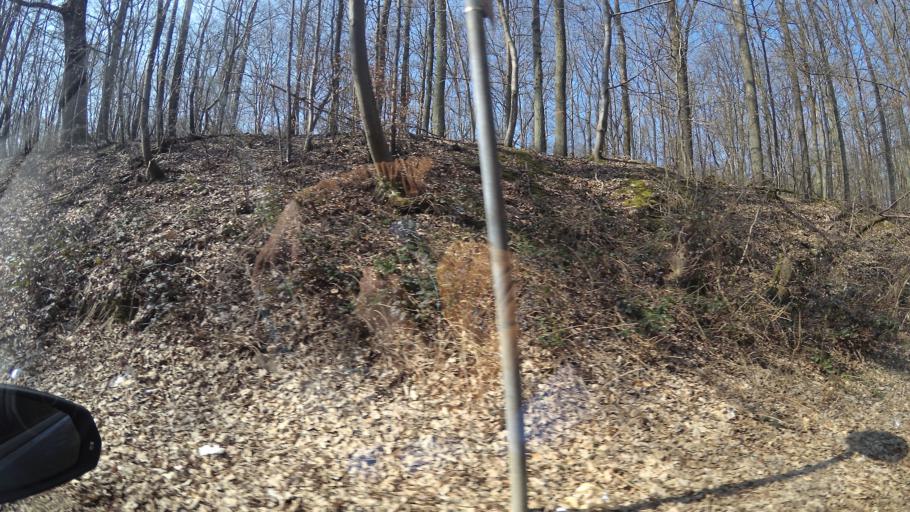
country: DE
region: Saarland
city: Friedrichsthal
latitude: 49.3192
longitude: 7.0841
